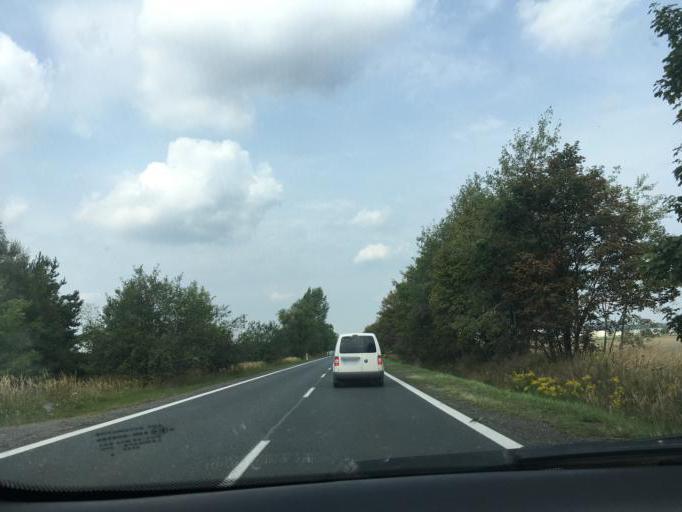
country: PL
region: Silesian Voivodeship
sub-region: Powiat bierunsko-ledzinski
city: Bierun
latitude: 50.0873
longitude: 19.1090
